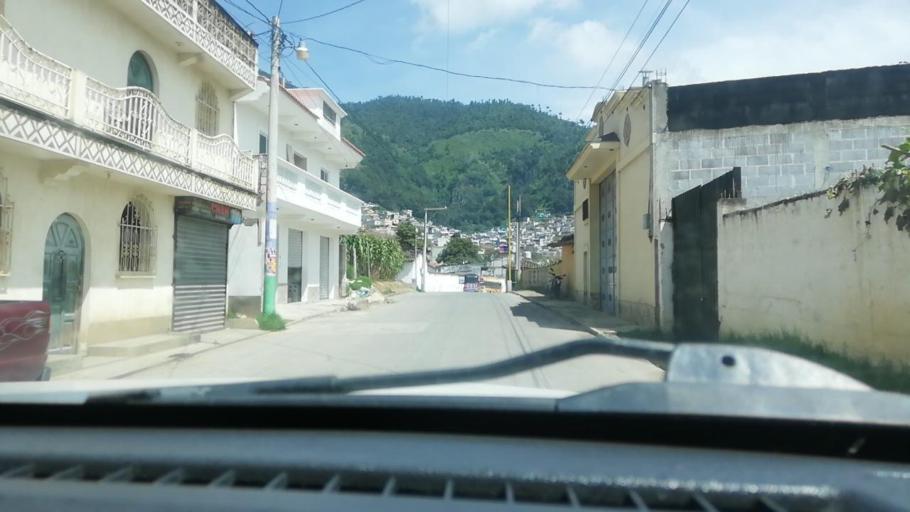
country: GT
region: Totonicapan
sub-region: Municipio de San Andres Xecul
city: San Andres Xecul
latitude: 14.9007
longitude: -91.4809
